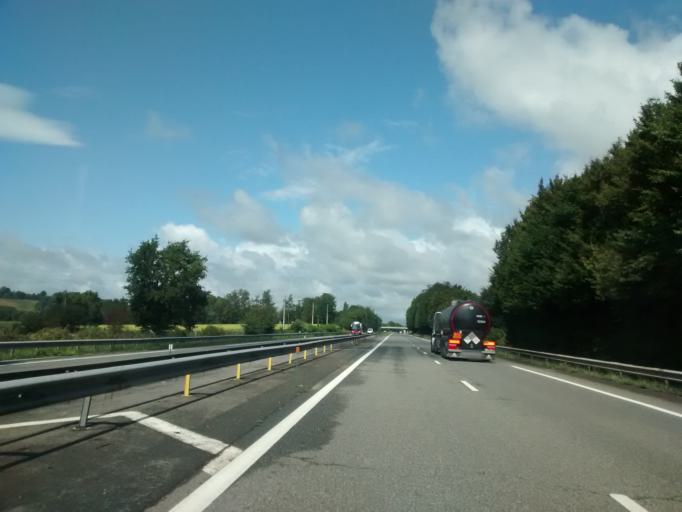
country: FR
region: Aquitaine
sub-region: Departement des Pyrenees-Atlantiques
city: Orthez
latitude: 43.4845
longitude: -0.8116
